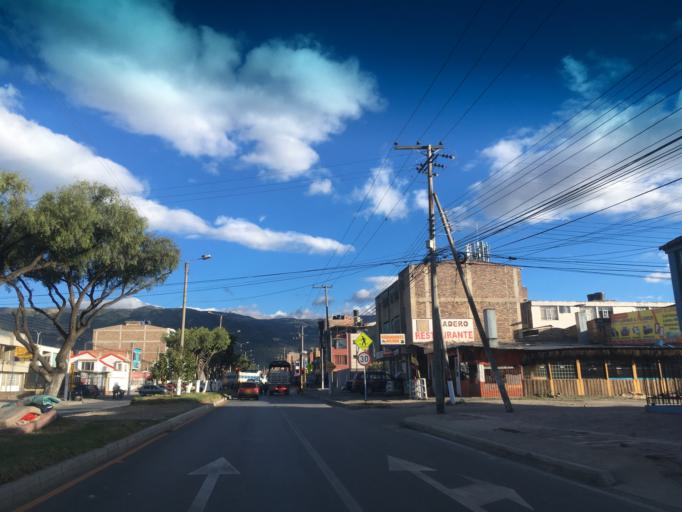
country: CO
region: Boyaca
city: Sogamoso
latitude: 5.7158
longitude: -72.9393
